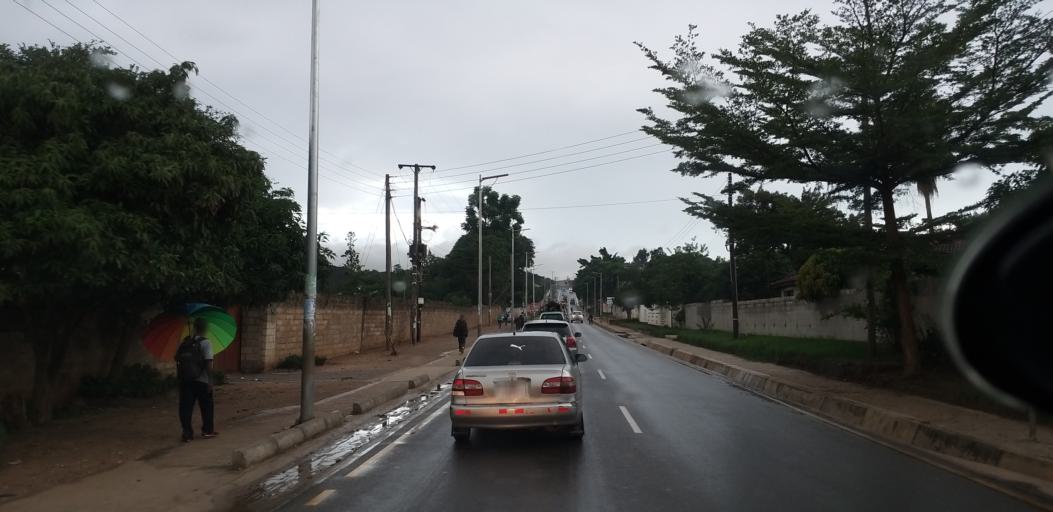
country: ZM
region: Lusaka
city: Lusaka
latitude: -15.4174
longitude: 28.3590
